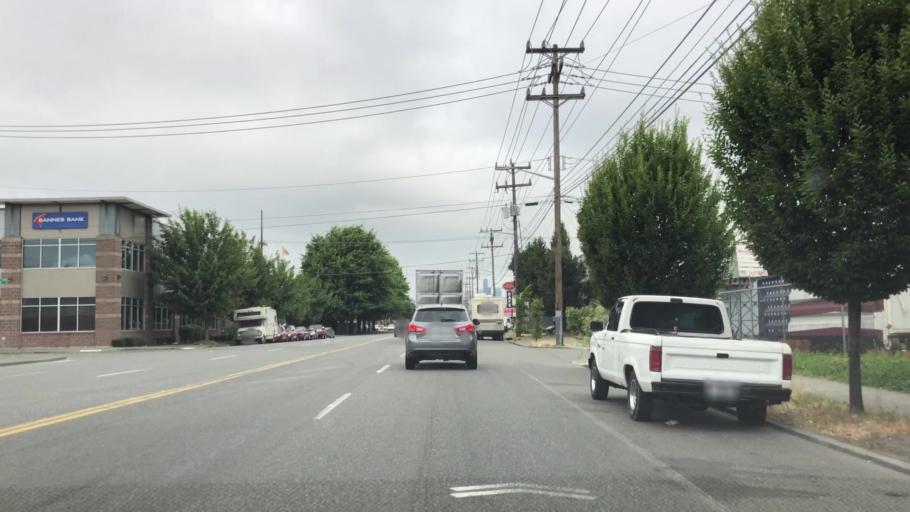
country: US
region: Washington
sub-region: King County
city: White Center
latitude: 47.5508
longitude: -122.3342
